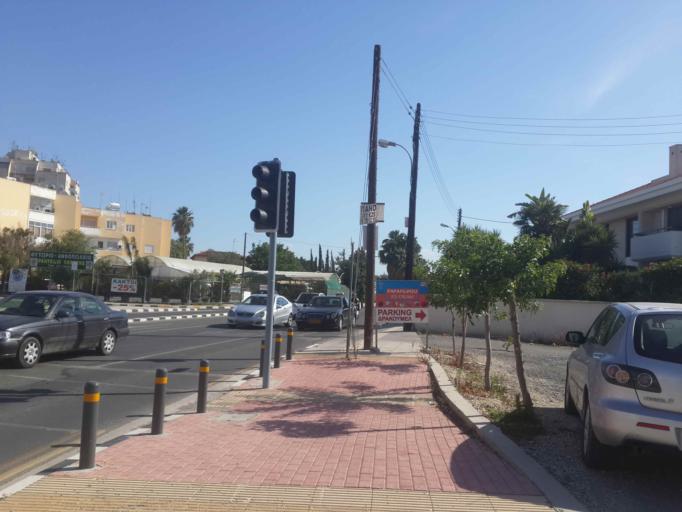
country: CY
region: Lefkosia
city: Nicosia
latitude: 35.1546
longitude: 33.3388
